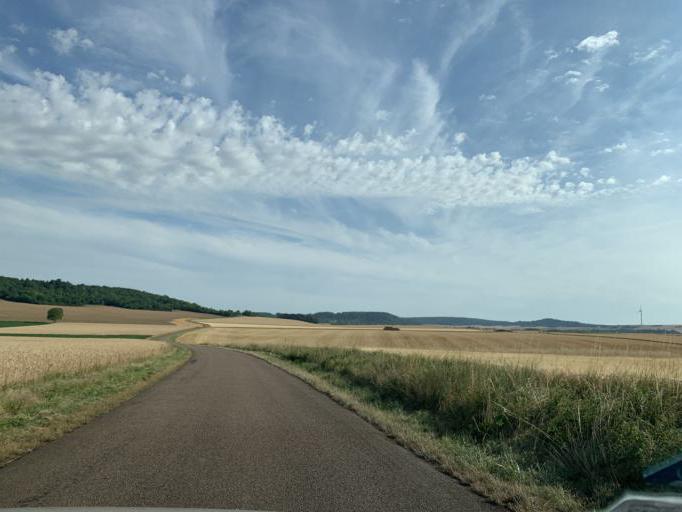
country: FR
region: Bourgogne
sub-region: Departement de la Nievre
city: Clamecy
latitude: 47.4565
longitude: 3.4247
